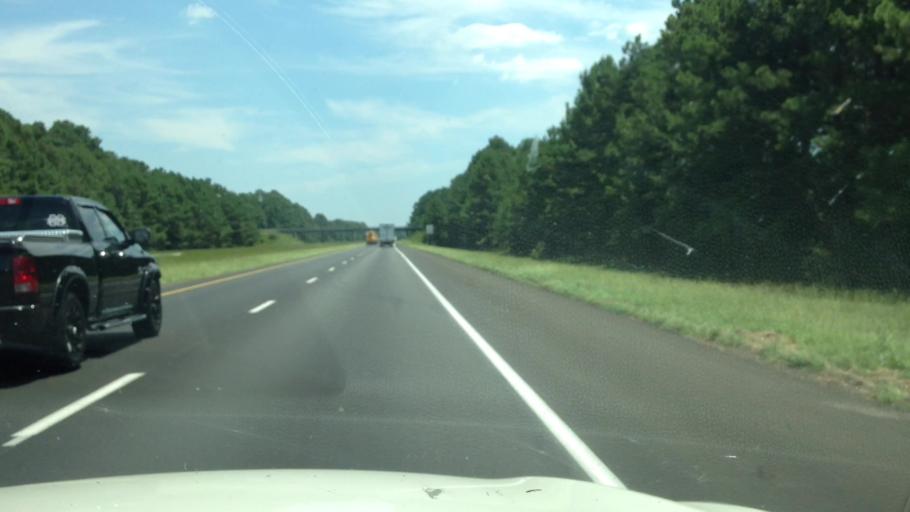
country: US
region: South Carolina
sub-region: Lee County
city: Bishopville
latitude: 34.1971
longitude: -80.1043
